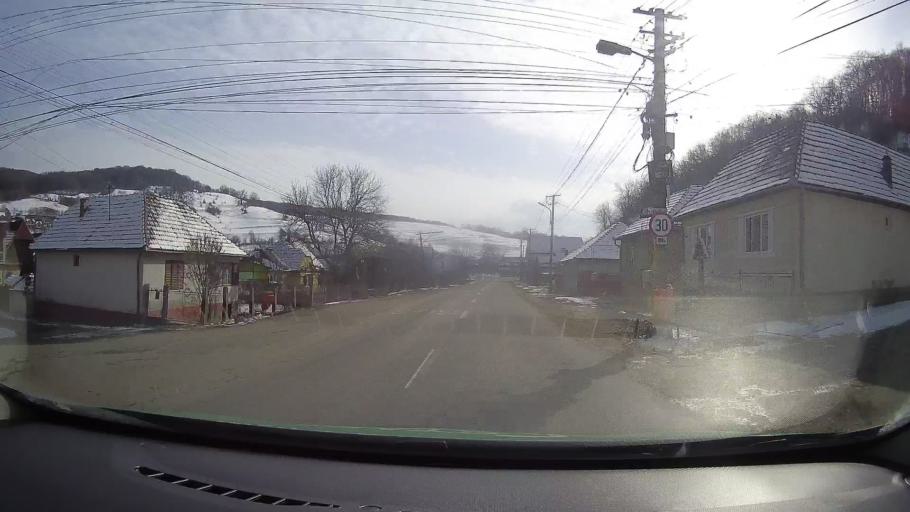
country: RO
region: Mures
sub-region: Municipiul Sighisoara
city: Sighisoara
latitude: 46.2067
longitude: 24.7780
